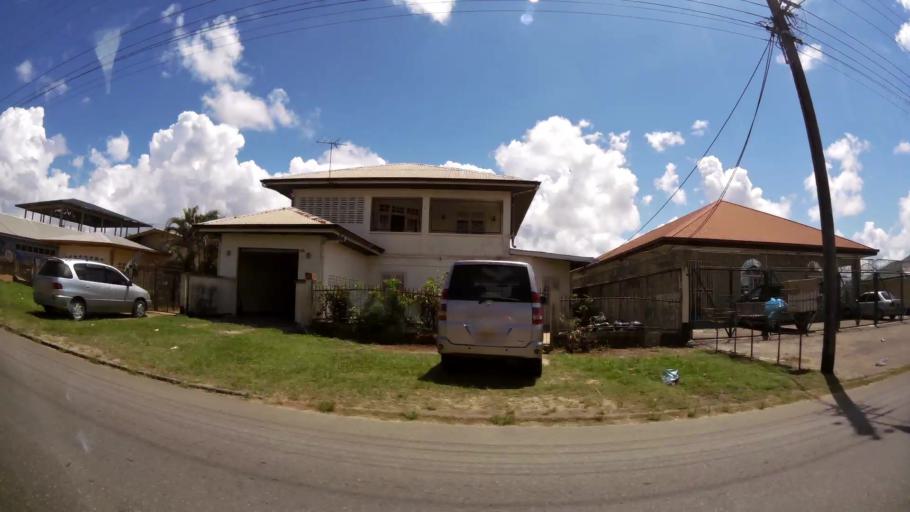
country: SR
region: Paramaribo
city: Paramaribo
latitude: 5.8580
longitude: -55.1457
